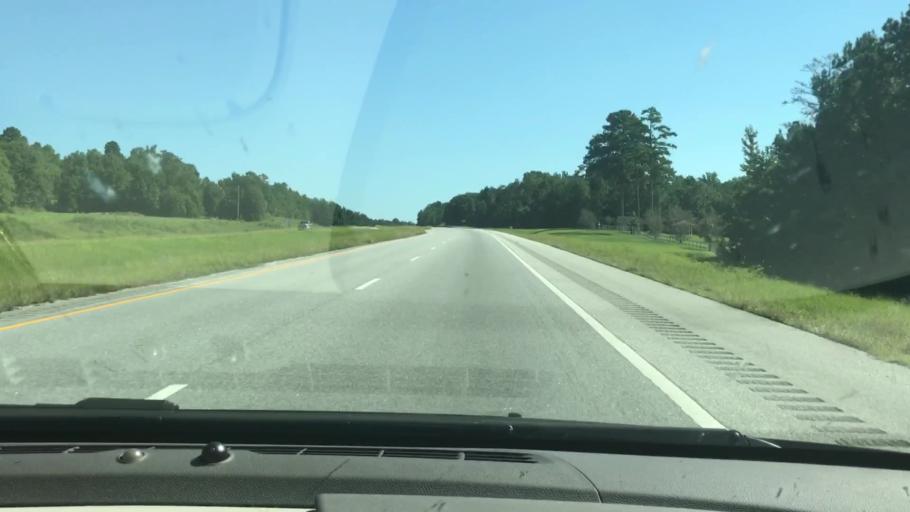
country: US
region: Alabama
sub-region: Russell County
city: Ladonia
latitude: 32.3959
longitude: -85.0677
